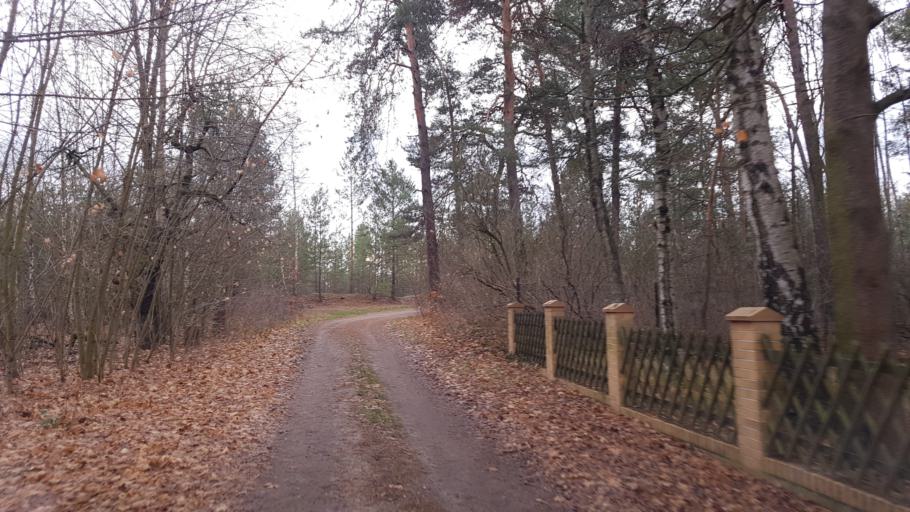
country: DE
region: Brandenburg
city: Sallgast
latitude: 51.5869
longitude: 13.8227
